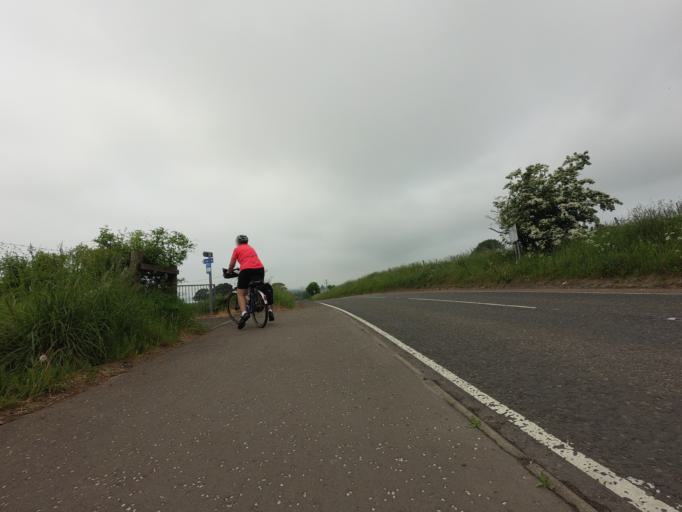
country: GB
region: Scotland
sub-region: Fife
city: Ballingry
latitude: 56.2230
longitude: -3.3535
